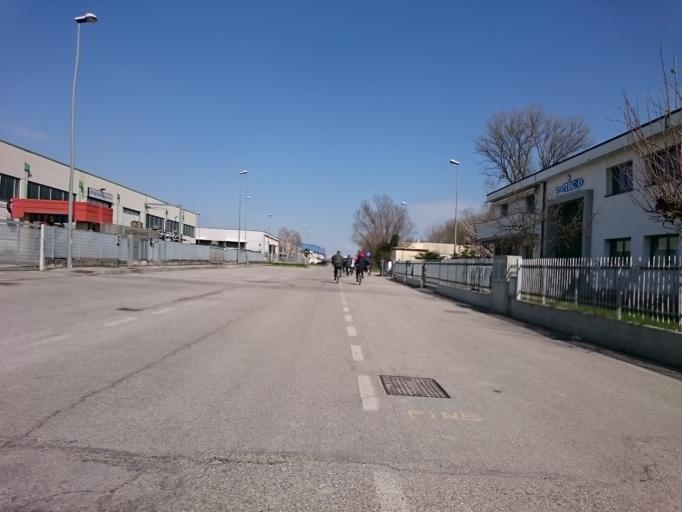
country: IT
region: Veneto
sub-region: Provincia di Padova
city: Terradura
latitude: 45.3424
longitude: 11.8320
